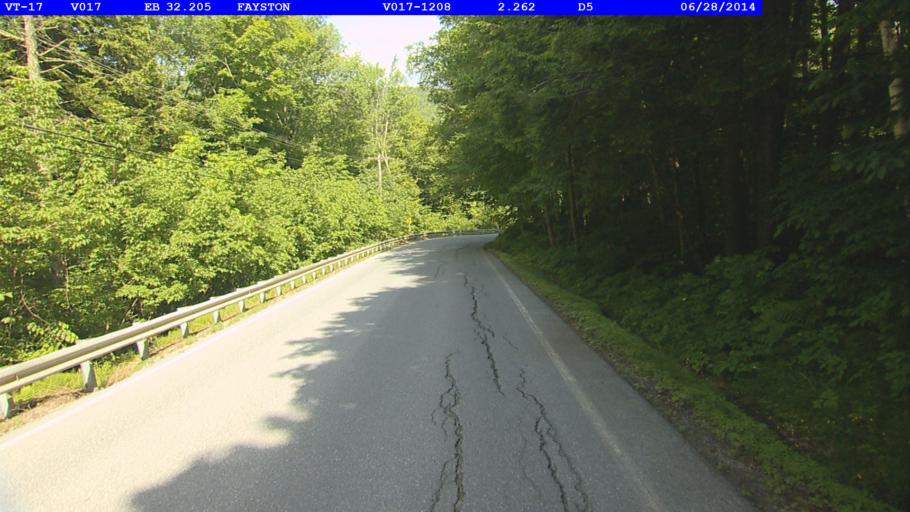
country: US
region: Vermont
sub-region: Addison County
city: Bristol
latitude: 44.2040
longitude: -72.8984
